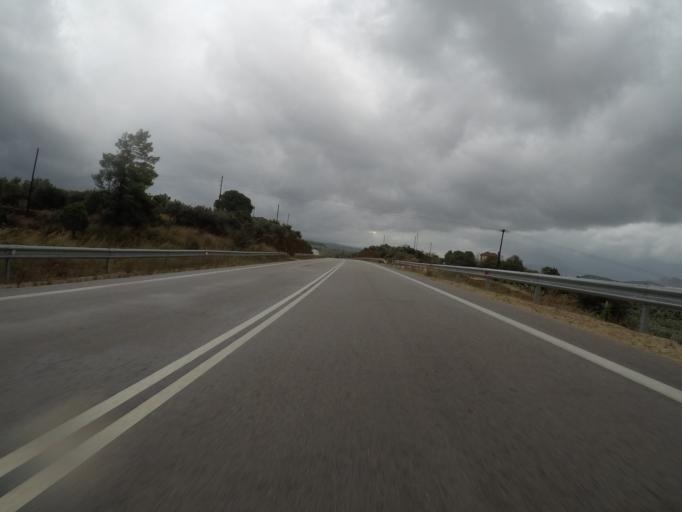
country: GR
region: Peloponnese
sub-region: Nomos Messinias
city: Gargalianoi
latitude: 37.0157
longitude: 21.6456
